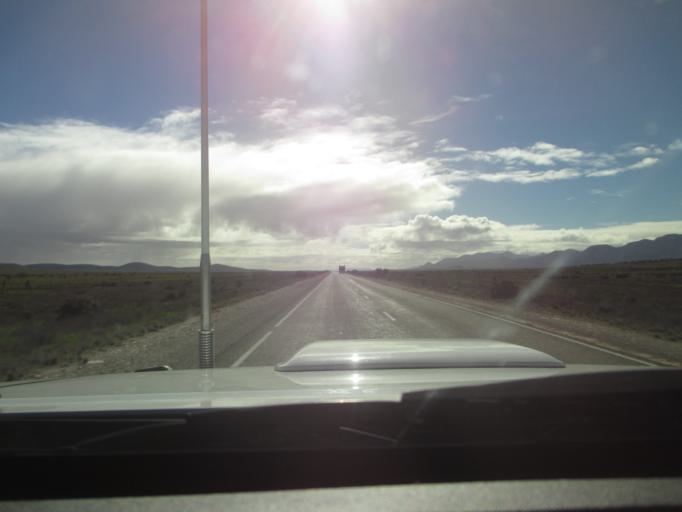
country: AU
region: South Australia
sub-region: Flinders Ranges
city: Quorn
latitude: -31.7085
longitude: 138.3533
